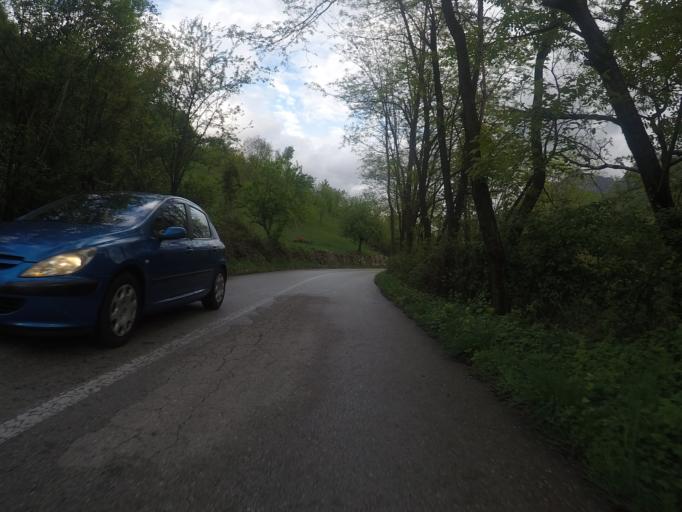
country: BA
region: Federation of Bosnia and Herzegovina
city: Siroki Brijeg
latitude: 43.5395
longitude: 17.5950
